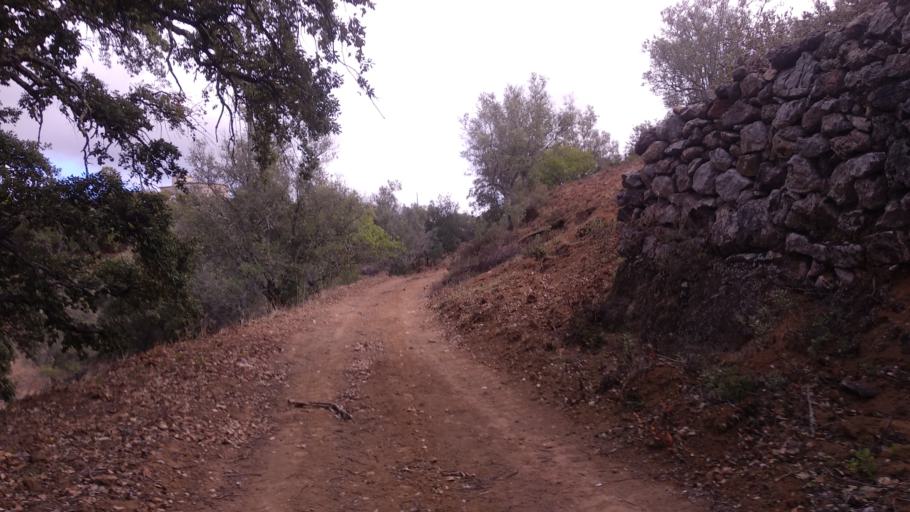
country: PT
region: Faro
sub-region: Sao Bras de Alportel
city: Sao Bras de Alportel
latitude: 37.1602
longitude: -7.9069
